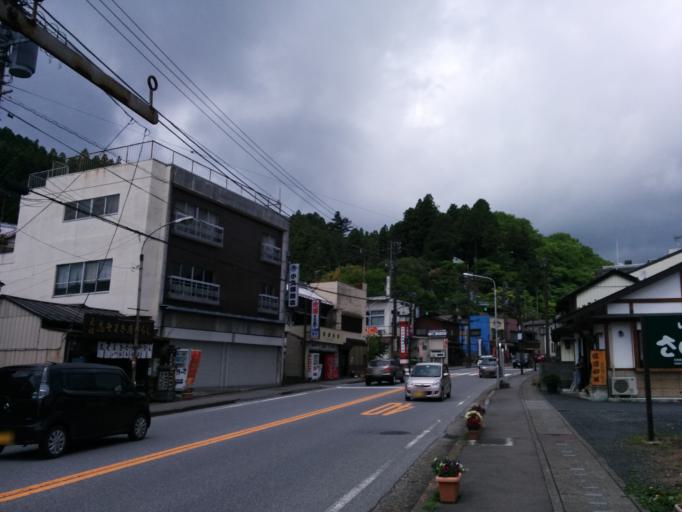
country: JP
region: Tochigi
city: Nikko
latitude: 36.7510
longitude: 139.6087
